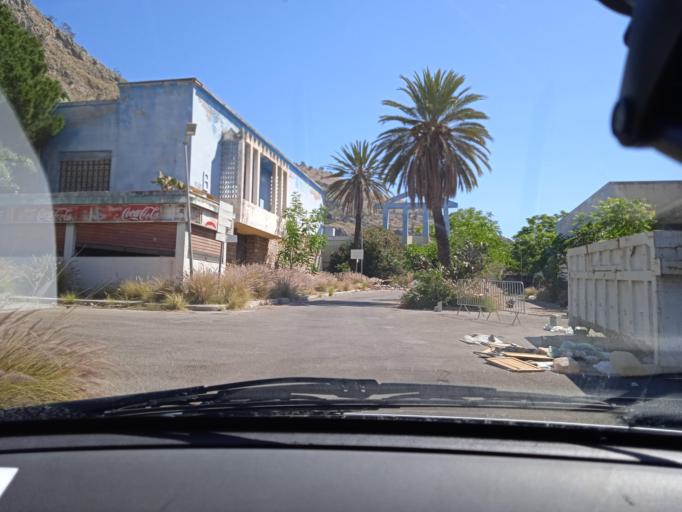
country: IT
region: Sicily
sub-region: Palermo
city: Palermo
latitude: 38.1474
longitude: 13.3558
